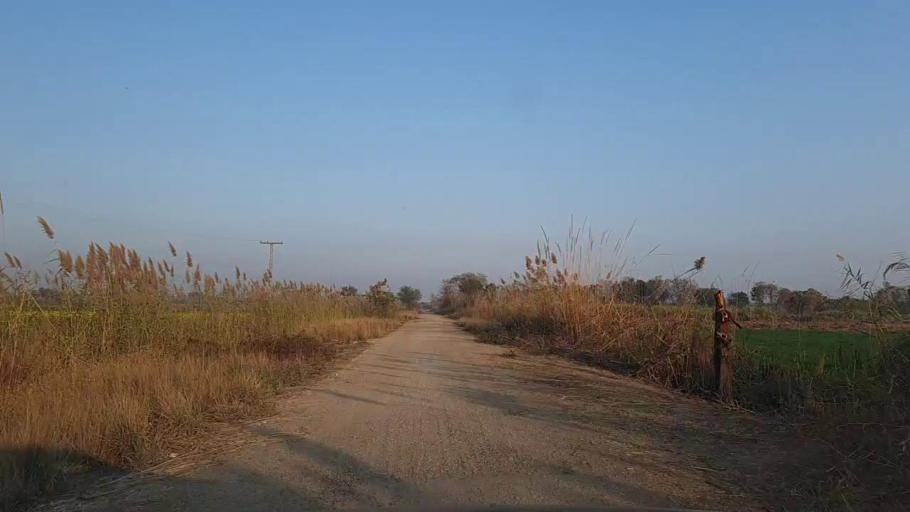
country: PK
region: Sindh
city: Daur
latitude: 26.4874
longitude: 68.4237
